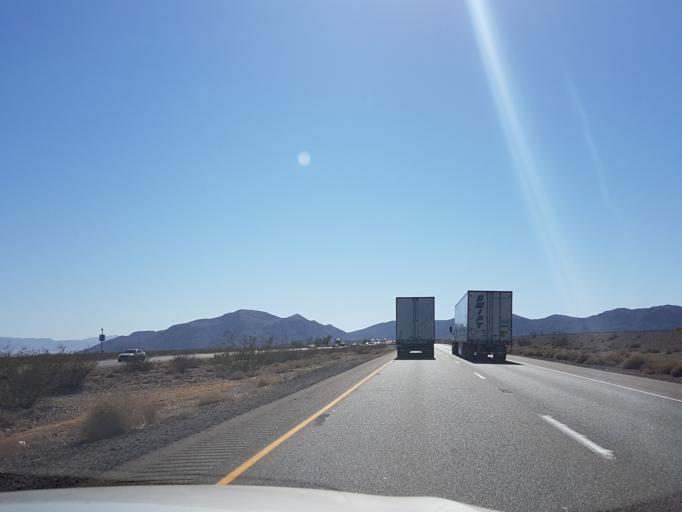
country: US
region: California
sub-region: San Bernardino County
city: Fort Irwin
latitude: 35.2226
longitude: -116.1079
